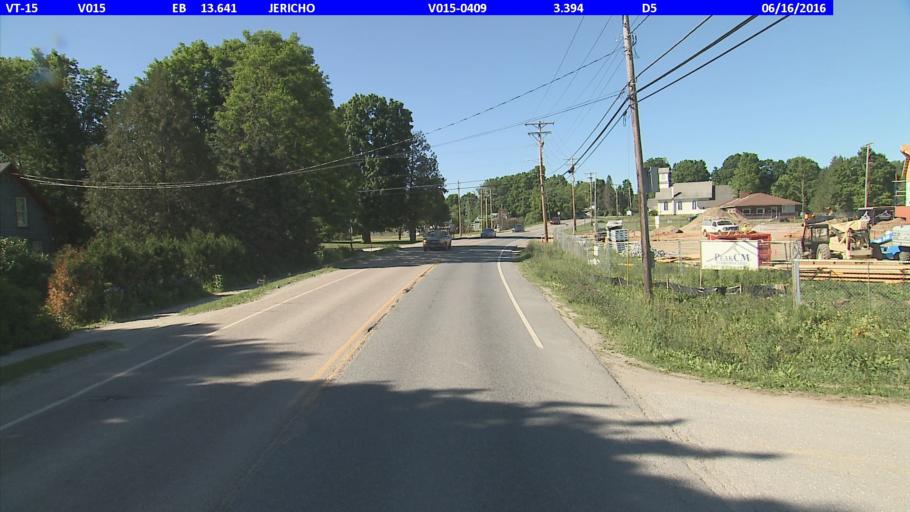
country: US
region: Vermont
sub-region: Chittenden County
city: Jericho
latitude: 44.5200
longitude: -72.9478
